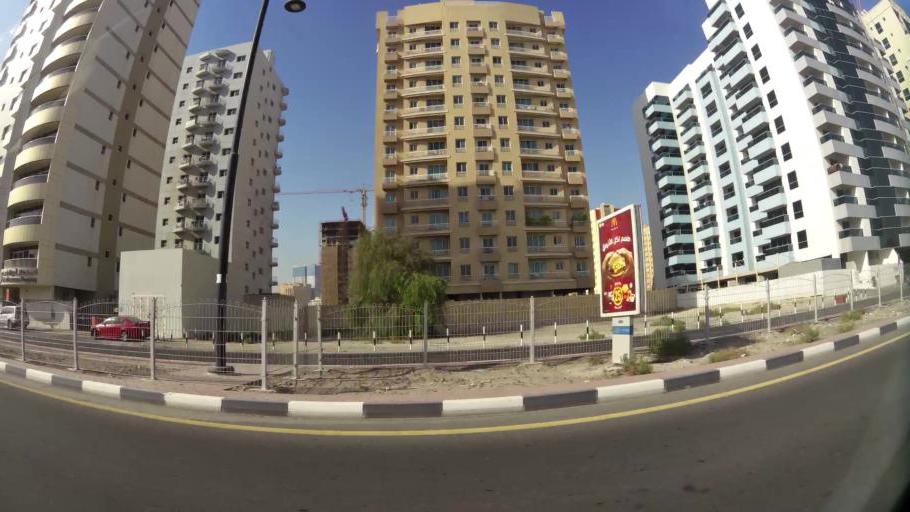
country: AE
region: Ash Shariqah
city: Sharjah
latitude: 25.2888
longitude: 55.3762
